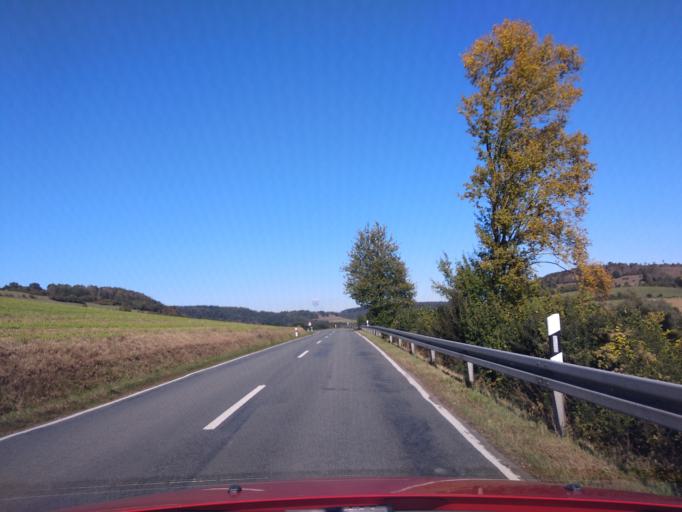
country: DE
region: North Rhine-Westphalia
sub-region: Regierungsbezirk Detmold
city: Hoexter
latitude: 51.7602
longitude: 9.2907
